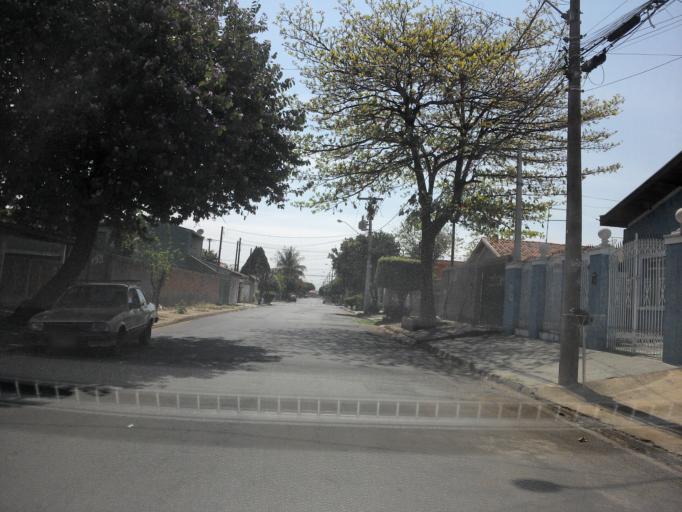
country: BR
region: Sao Paulo
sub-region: Hortolandia
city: Hortolandia
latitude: -22.8886
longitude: -47.2315
